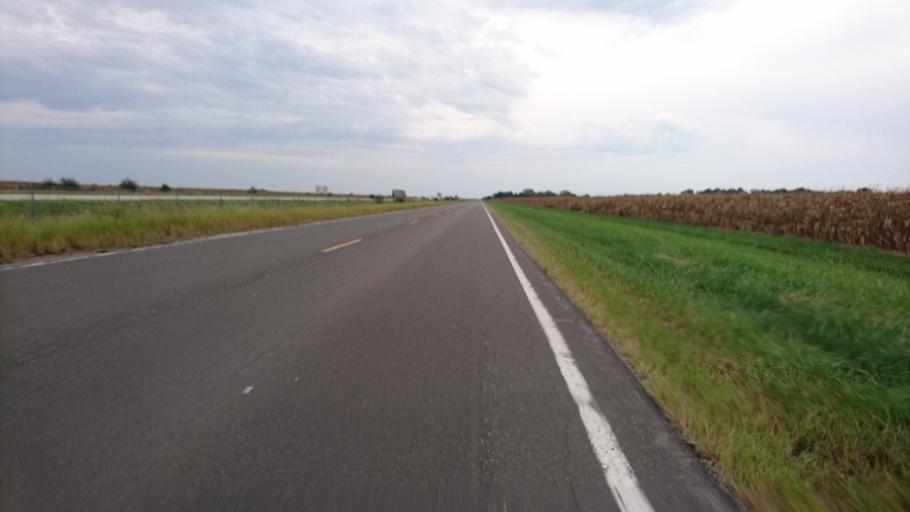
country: US
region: Illinois
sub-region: Sangamon County
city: Chatham
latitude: 39.6676
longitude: -89.6481
